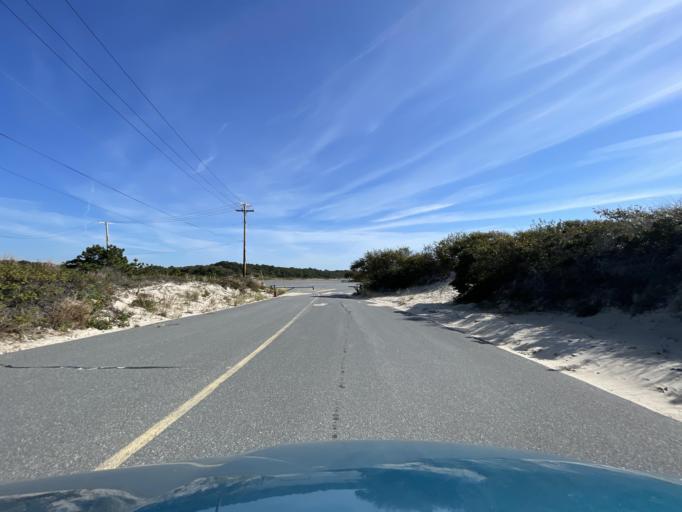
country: US
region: Massachusetts
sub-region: Bristol County
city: Head of Westport
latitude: 41.5061
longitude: -71.0526
